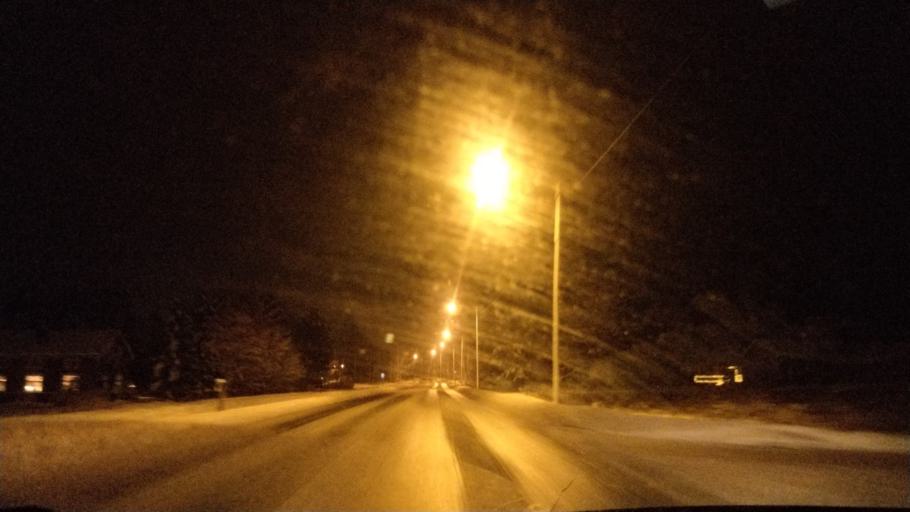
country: FI
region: Lapland
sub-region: Rovaniemi
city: Rovaniemi
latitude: 66.3941
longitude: 25.3821
